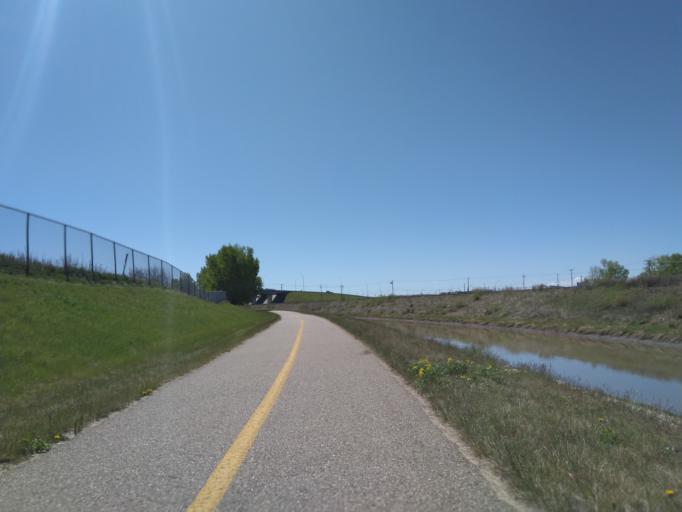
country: CA
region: Alberta
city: Calgary
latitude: 50.9681
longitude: -113.9853
